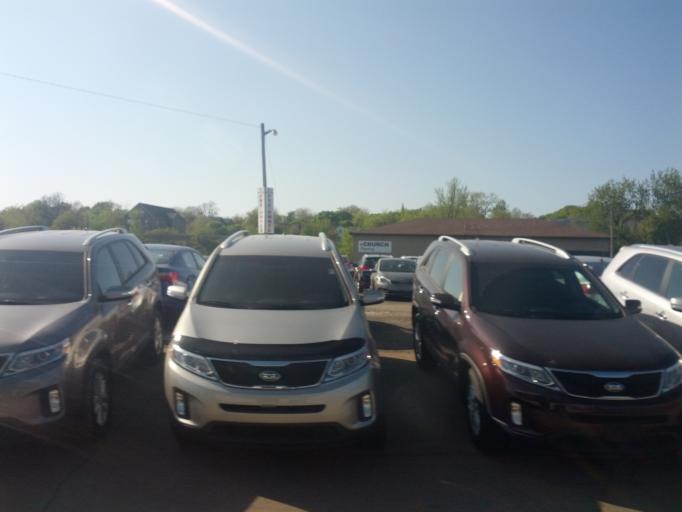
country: CA
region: New Brunswick
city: Moncton
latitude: 46.1008
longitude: -64.7733
